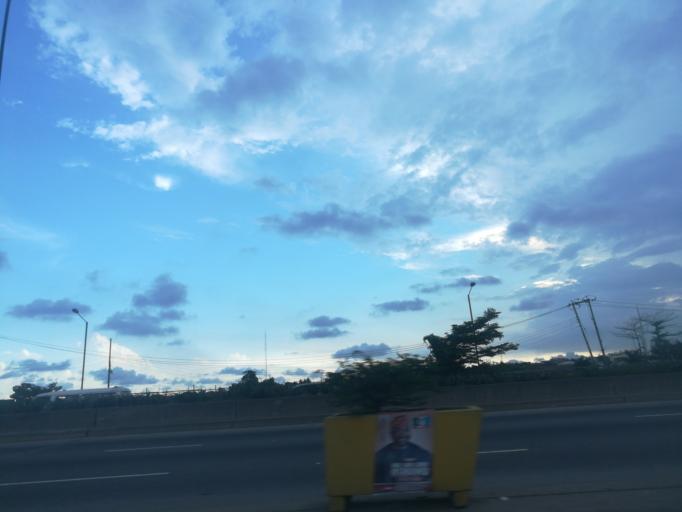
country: NG
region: Lagos
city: Somolu
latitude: 6.5532
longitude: 3.3744
